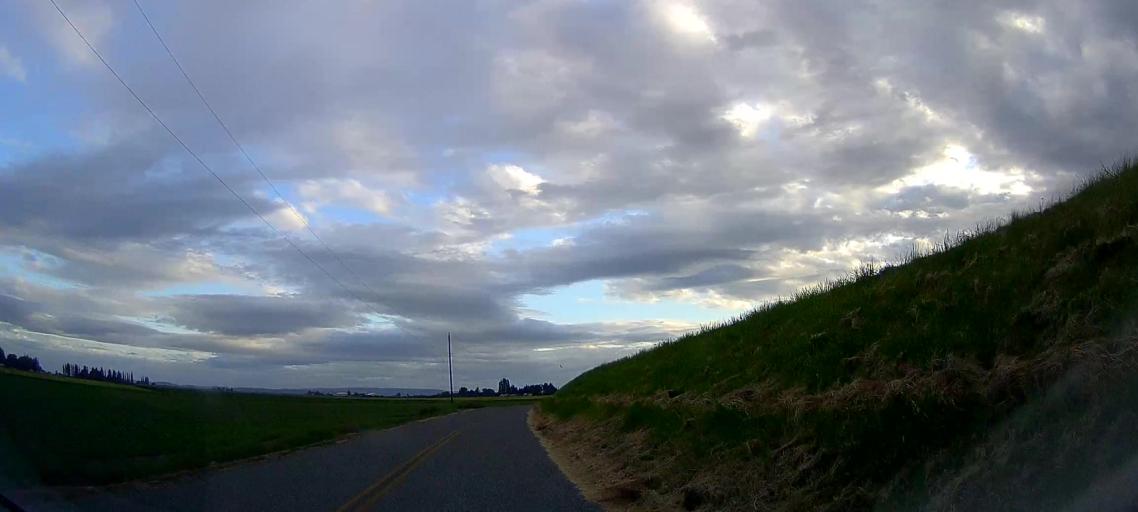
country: US
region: Washington
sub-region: Skagit County
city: Mount Vernon
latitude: 48.3693
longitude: -122.3946
